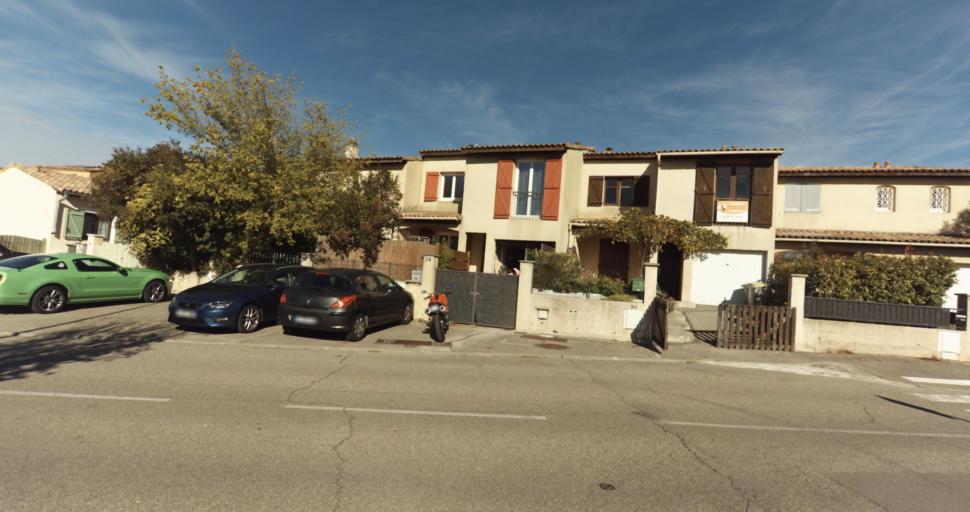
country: FR
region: Provence-Alpes-Cote d'Azur
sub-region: Departement des Bouches-du-Rhone
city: Venelles
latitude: 43.5961
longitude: 5.4798
